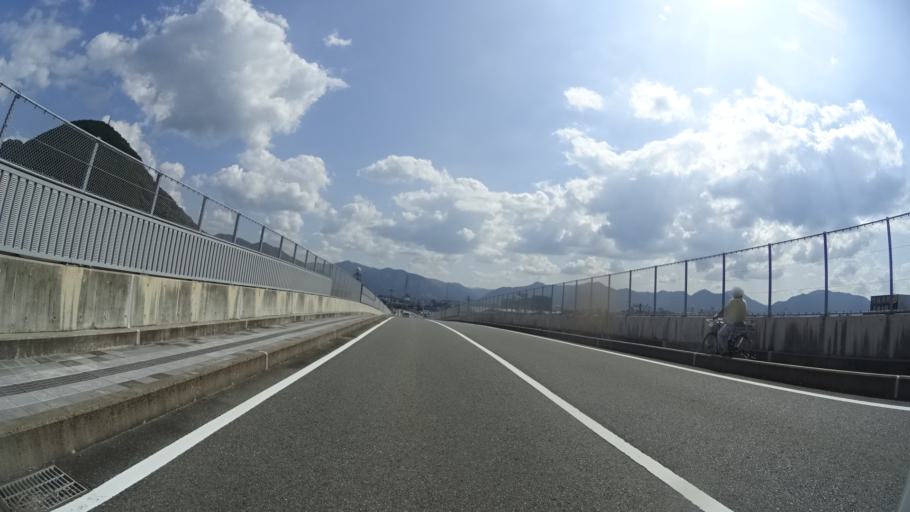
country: JP
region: Yamaguchi
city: Hagi
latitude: 34.4239
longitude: 131.4126
